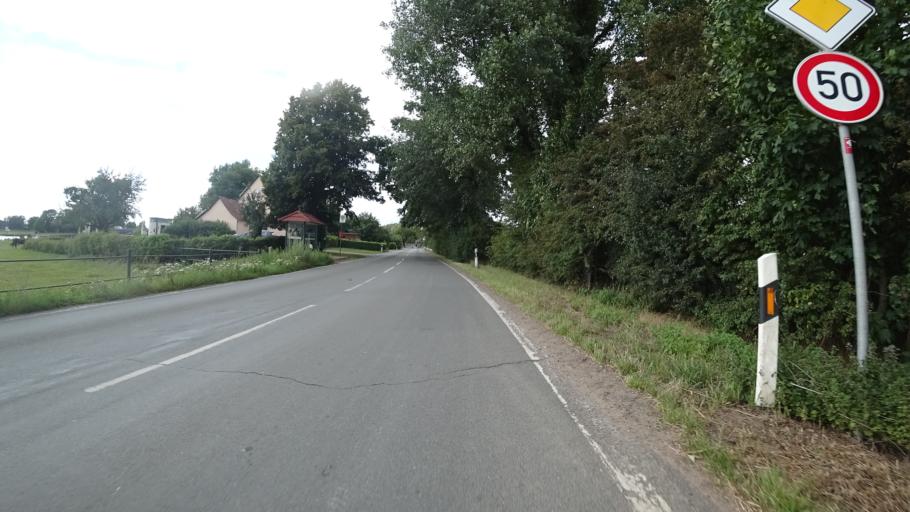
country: DE
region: Lower Saxony
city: Leese
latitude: 52.4806
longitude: 9.0853
